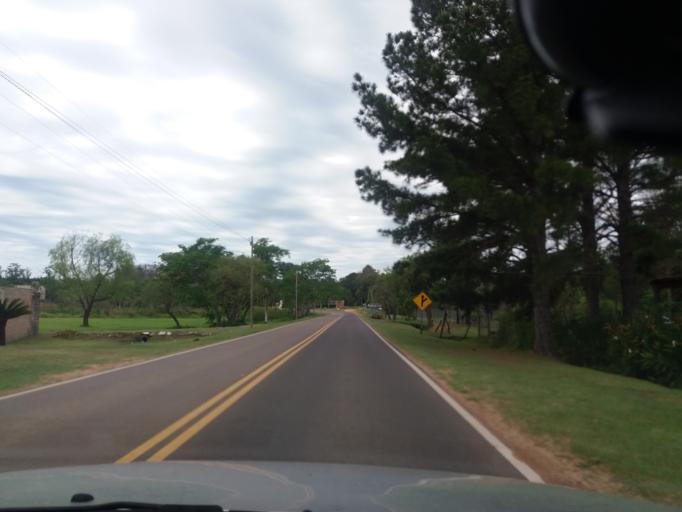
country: AR
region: Corrientes
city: San Luis del Palmar
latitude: -27.4597
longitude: -58.6676
